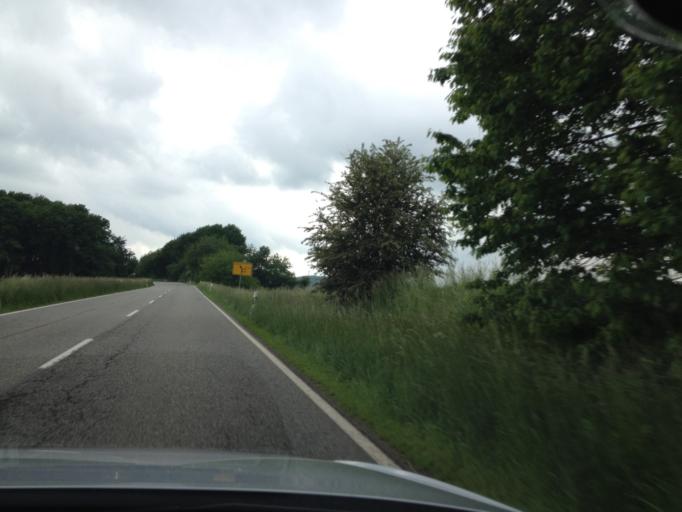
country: DE
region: Rheinland-Pfalz
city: Hahnweiler
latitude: 49.5268
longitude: 7.2105
